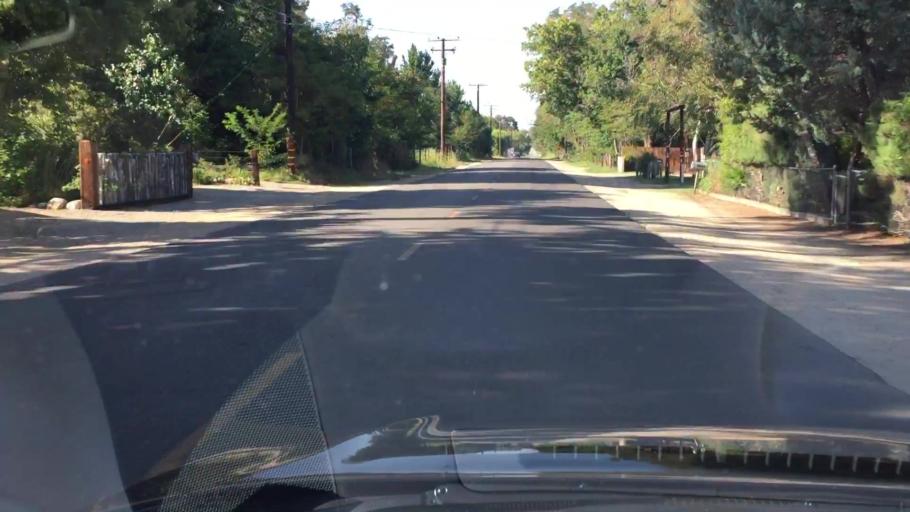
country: US
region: California
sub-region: Inyo County
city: Dixon Lane-Meadow Creek
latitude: 37.3724
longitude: -118.4321
